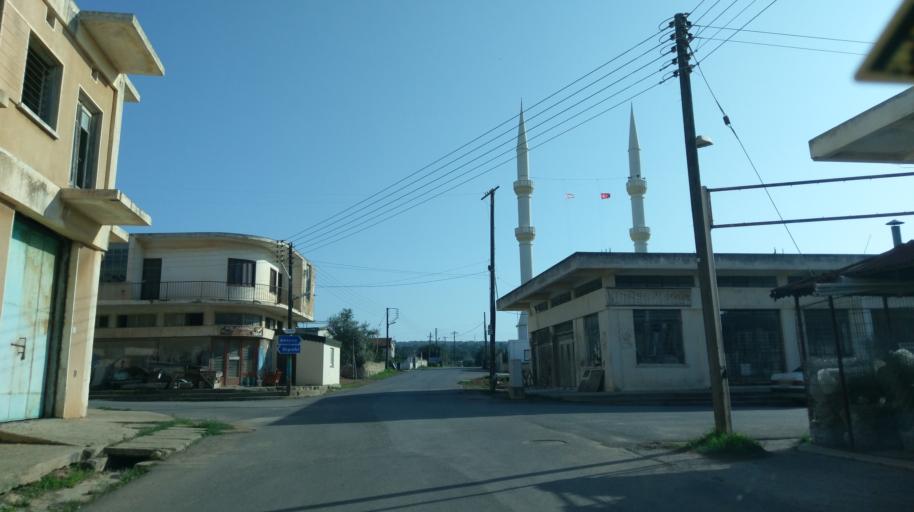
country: CY
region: Ammochostos
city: Leonarisso
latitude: 35.5339
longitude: 34.1890
